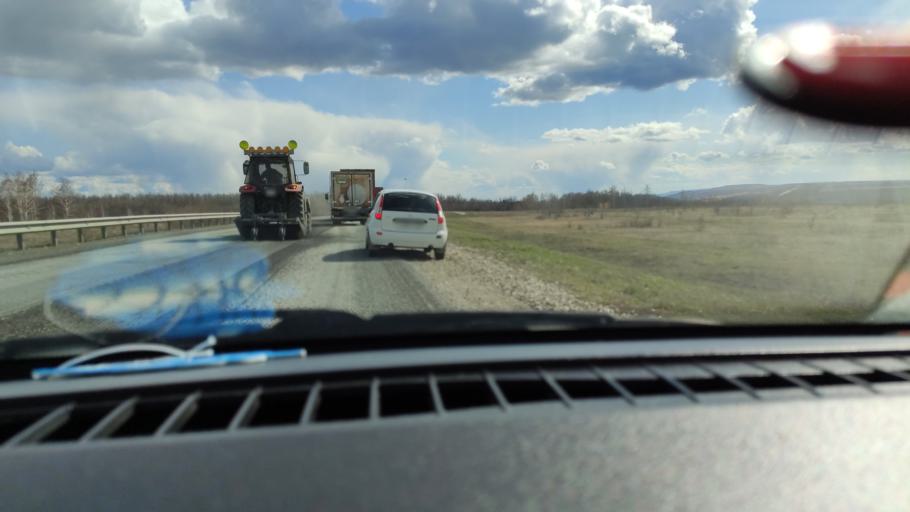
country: RU
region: Saratov
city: Dukhovnitskoye
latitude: 52.7128
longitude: 48.2664
